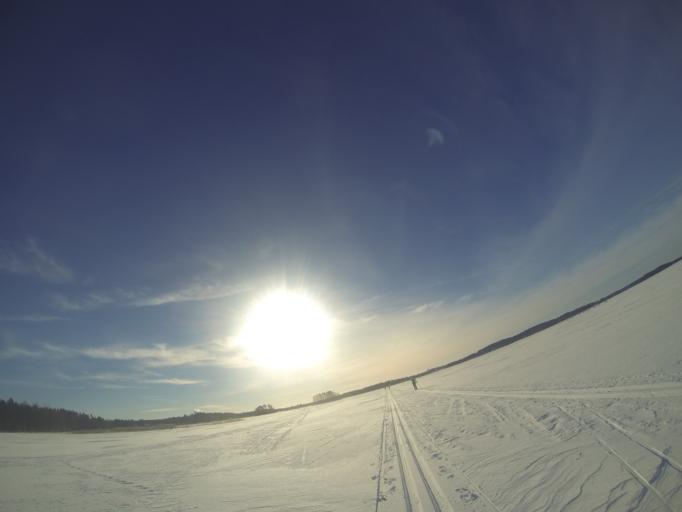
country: FI
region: Southern Savonia
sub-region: Savonlinna
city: Savonlinna
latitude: 61.8914
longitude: 28.9070
